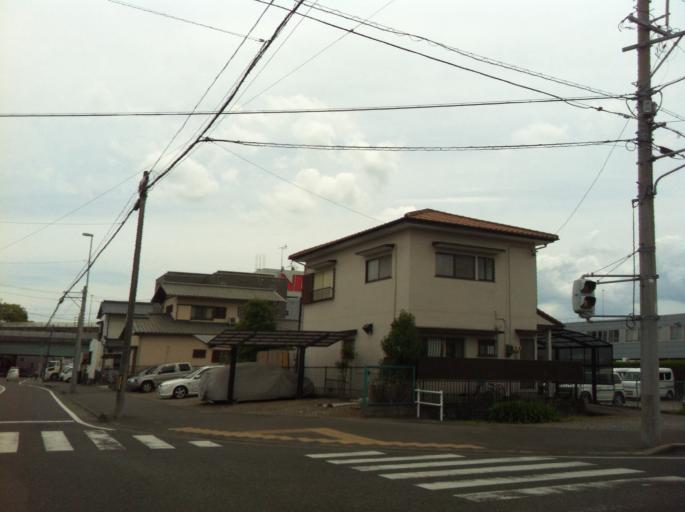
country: JP
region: Shizuoka
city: Shizuoka-shi
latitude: 35.0544
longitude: 138.4256
